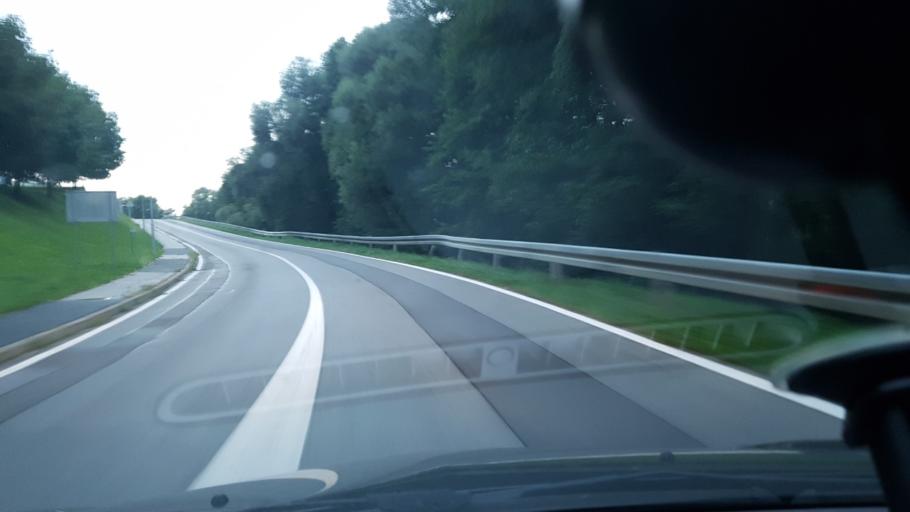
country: SI
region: Rogatec
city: Rogatec
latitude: 46.2227
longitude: 15.7128
